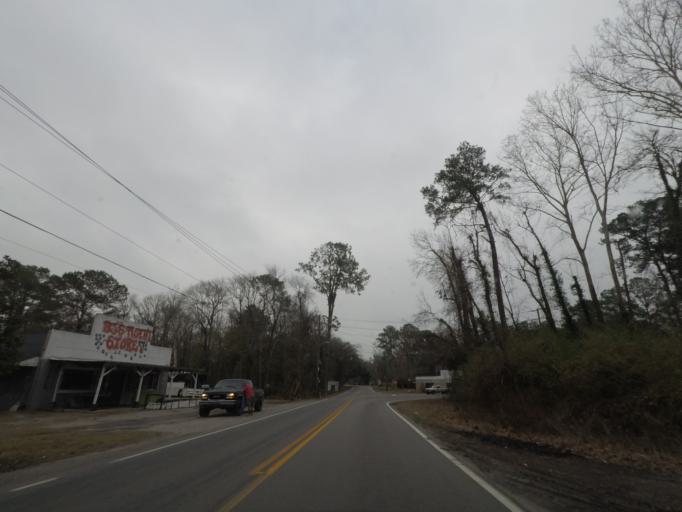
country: US
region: South Carolina
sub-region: Charleston County
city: Ravenel
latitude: 32.7210
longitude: -80.3488
